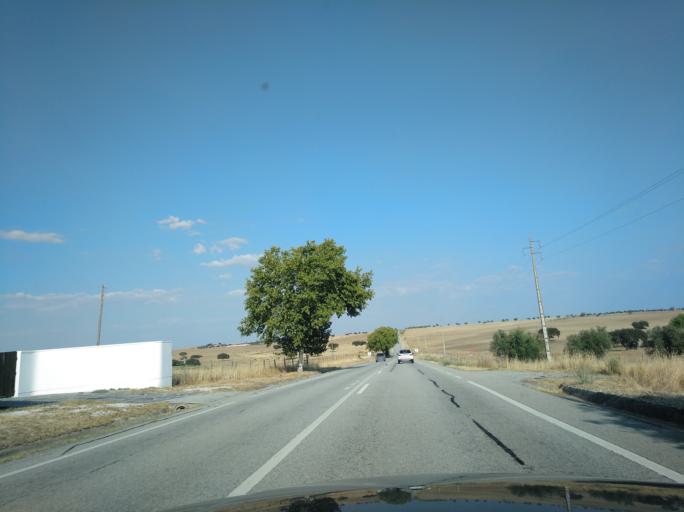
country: PT
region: Evora
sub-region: Mourao
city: Mourao
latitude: 38.3815
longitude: -7.2965
